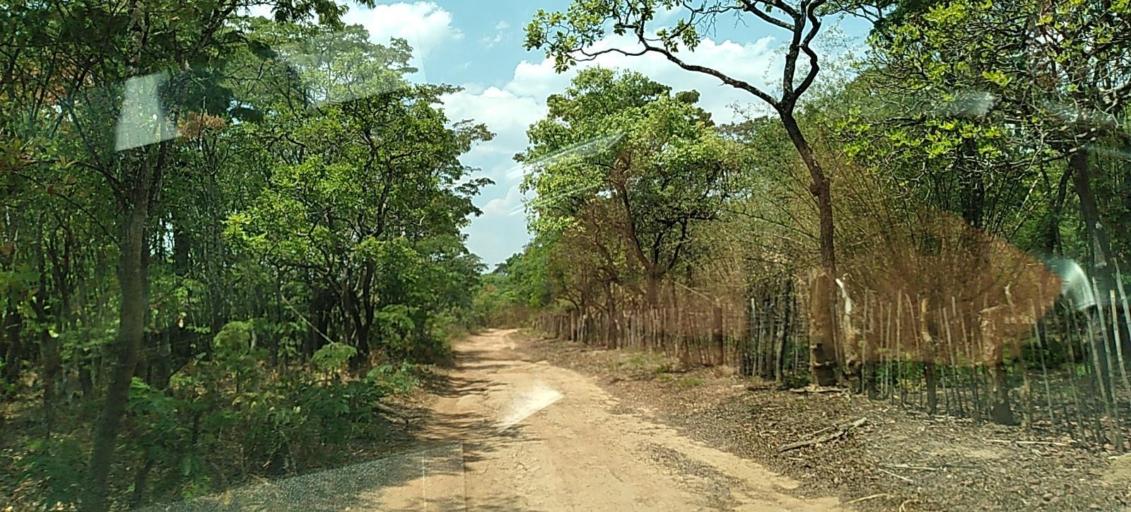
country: ZM
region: Copperbelt
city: Chililabombwe
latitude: -12.4838
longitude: 27.6420
